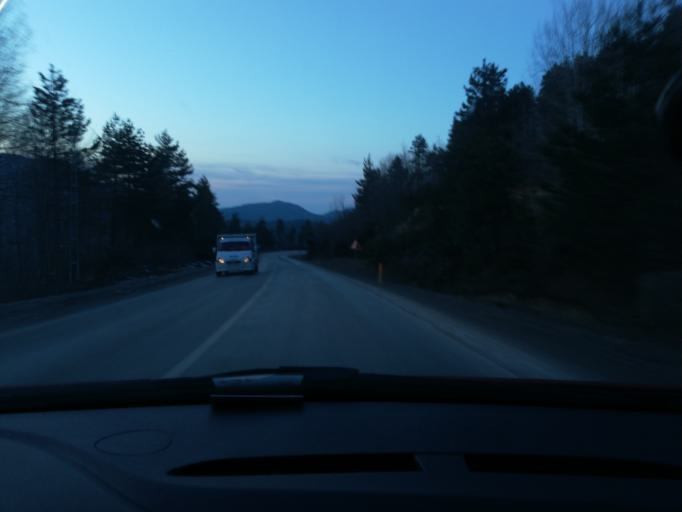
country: TR
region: Kastamonu
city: Kure
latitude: 41.8947
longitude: 33.7074
